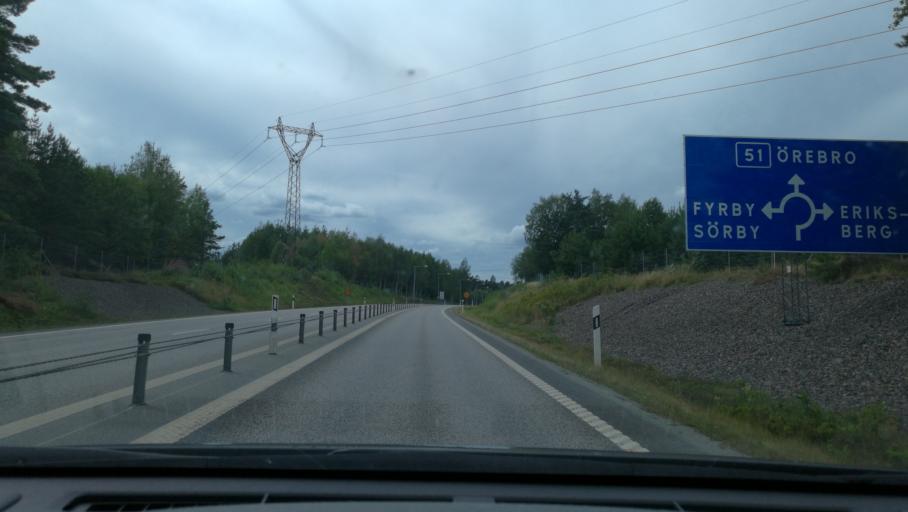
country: SE
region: OEstergoetland
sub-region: Norrkopings Kommun
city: Jursla
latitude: 58.6349
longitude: 16.1084
